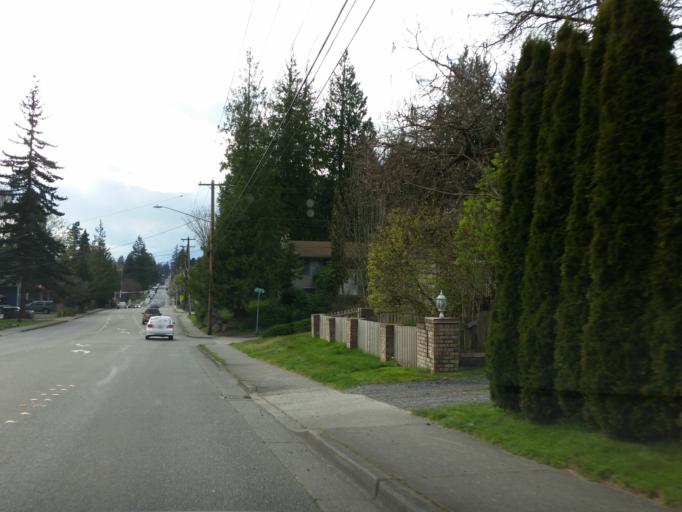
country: US
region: Washington
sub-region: Snohomish County
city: Alderwood Manor
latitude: 47.8283
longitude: -122.2885
